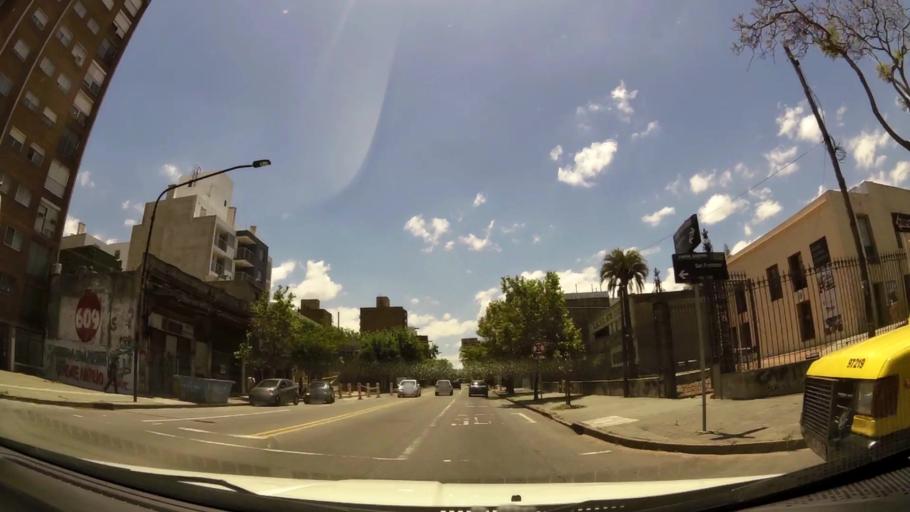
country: UY
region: Montevideo
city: Montevideo
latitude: -34.8807
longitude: -56.1954
